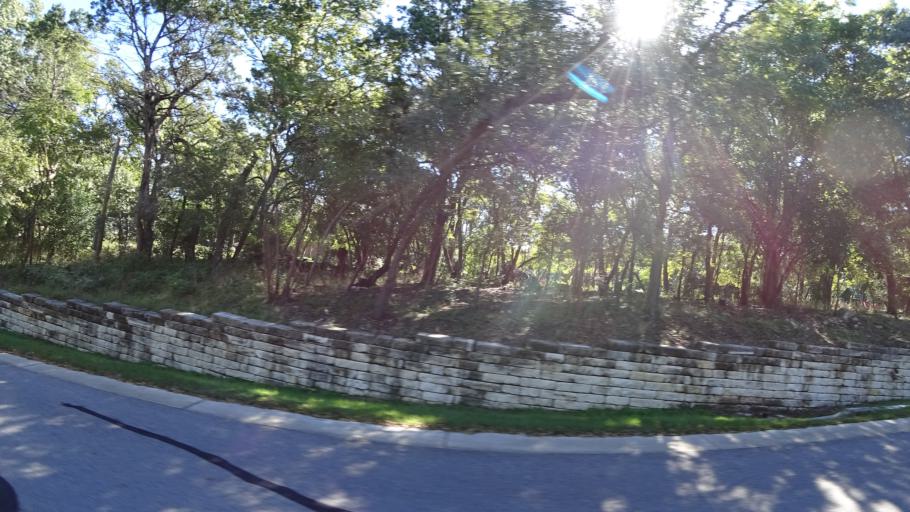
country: US
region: Texas
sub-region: Travis County
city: Rollingwood
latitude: 30.2237
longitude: -97.8103
